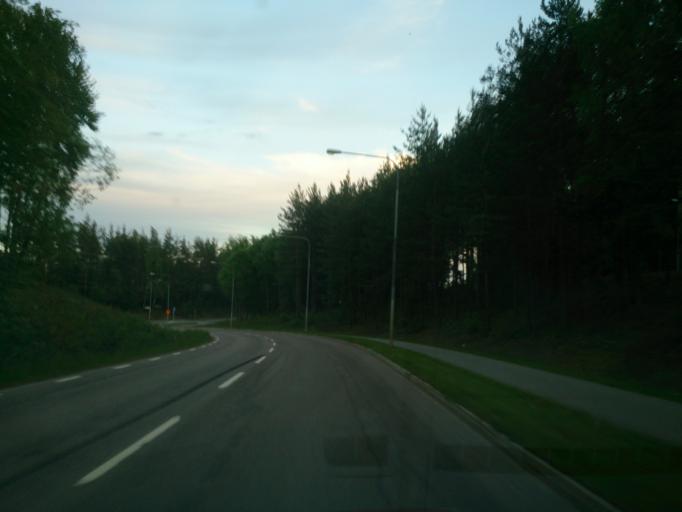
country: SE
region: OEstergoetland
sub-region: Linkopings Kommun
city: Malmslatt
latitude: 58.4066
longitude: 15.5512
